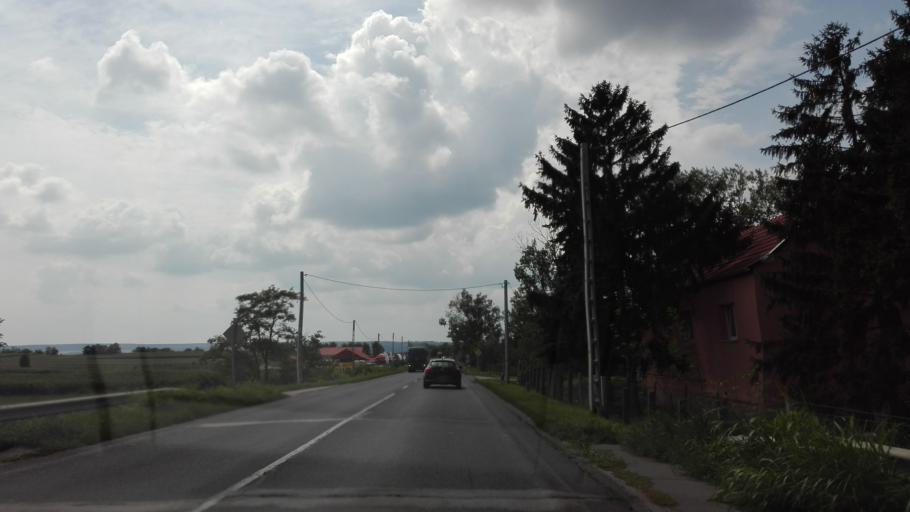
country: HU
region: Fejer
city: Cece
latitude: 46.7682
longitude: 18.6158
